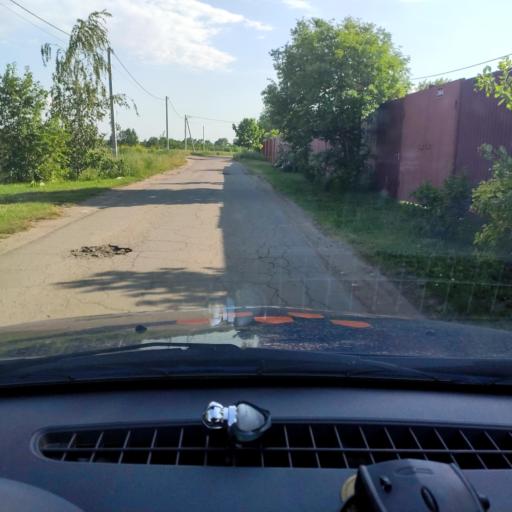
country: RU
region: Voronezj
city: Podkletnoye
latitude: 51.6194
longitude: 39.4466
